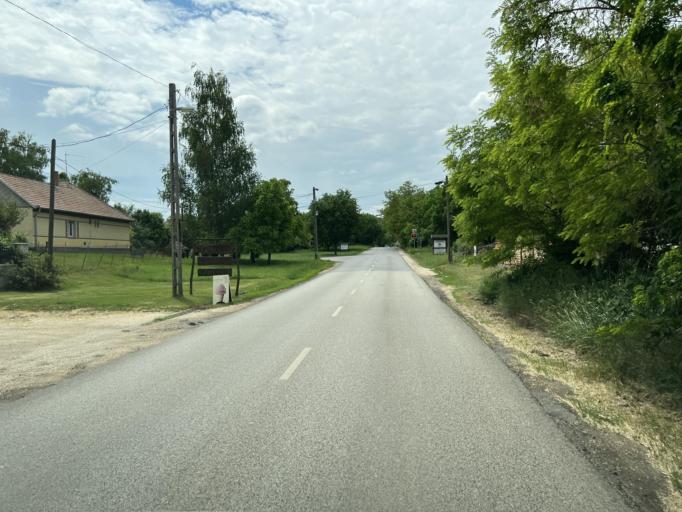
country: HU
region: Pest
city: Koka
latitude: 47.4925
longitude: 19.5837
